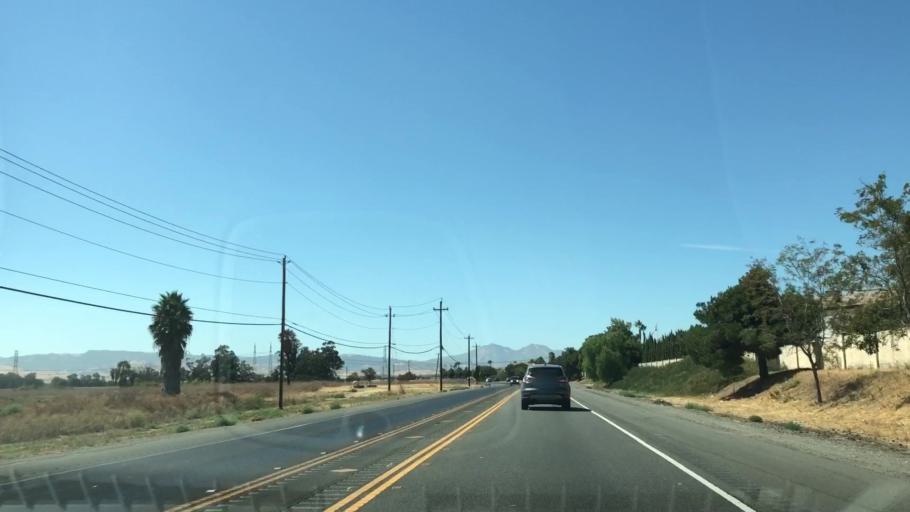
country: US
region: California
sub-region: Contra Costa County
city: Discovery Bay
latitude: 37.8901
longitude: -121.6064
